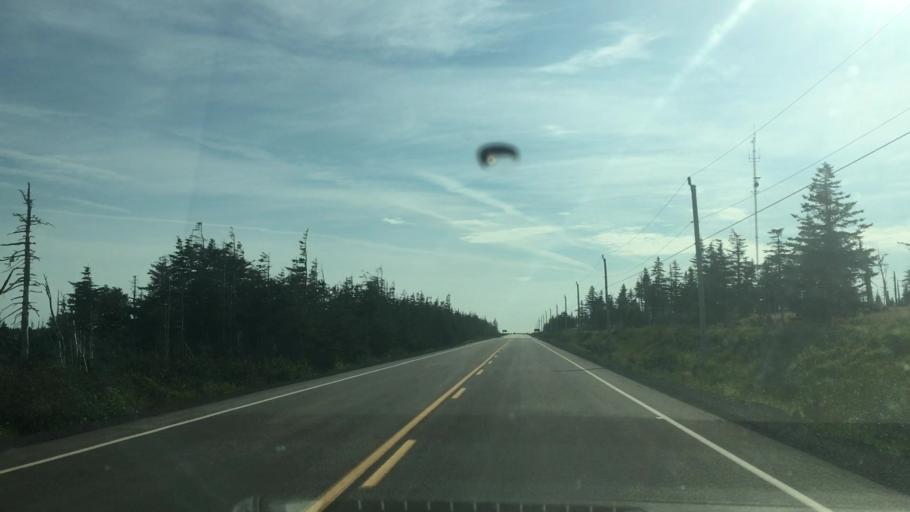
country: CA
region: Nova Scotia
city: Sydney Mines
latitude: 46.8197
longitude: -60.6675
